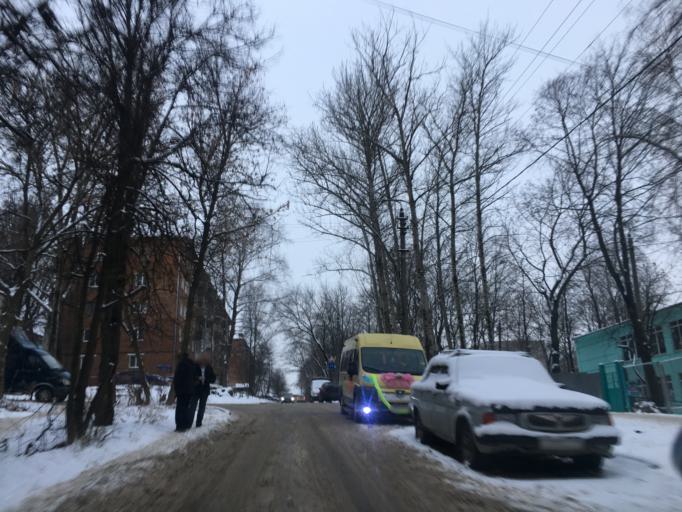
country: RU
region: Tula
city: Mendeleyevskiy
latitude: 54.1662
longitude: 37.5693
